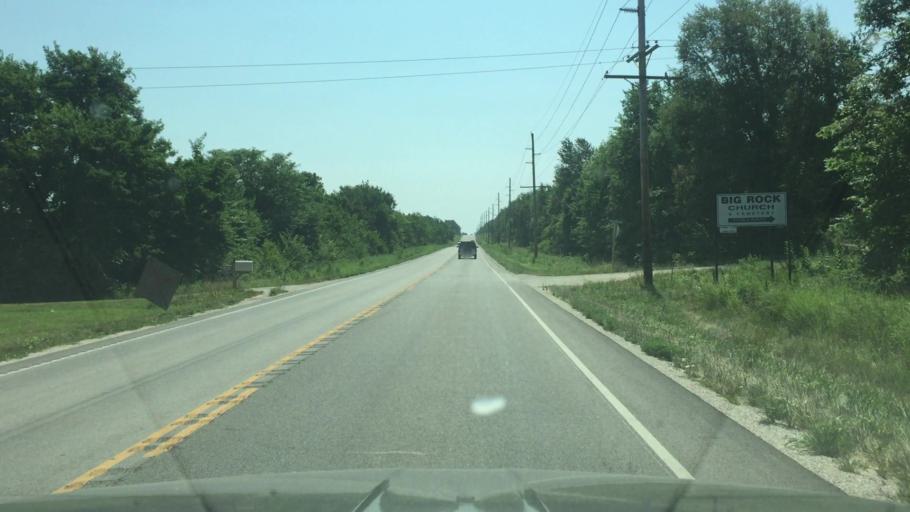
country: US
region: Missouri
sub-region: Morgan County
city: Versailles
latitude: 38.4007
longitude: -92.7421
